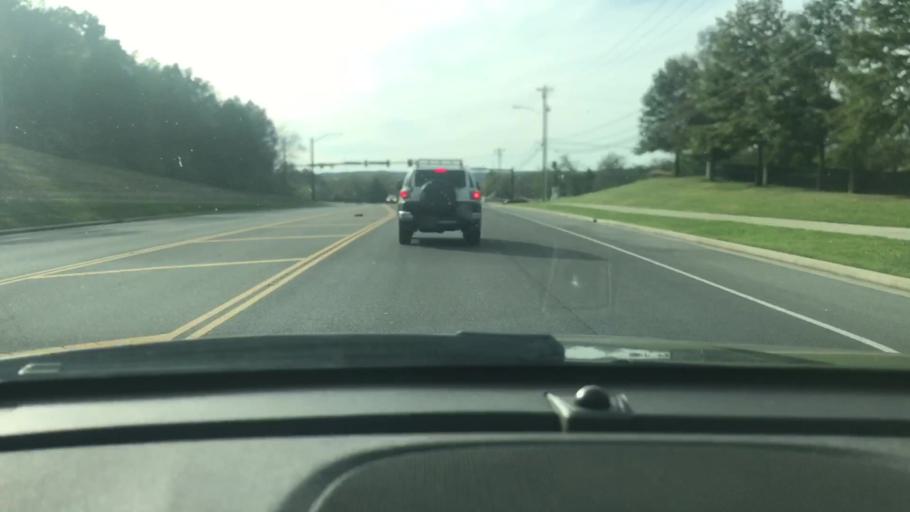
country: US
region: Tennessee
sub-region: Williamson County
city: Franklin
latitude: 35.9304
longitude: -86.9056
